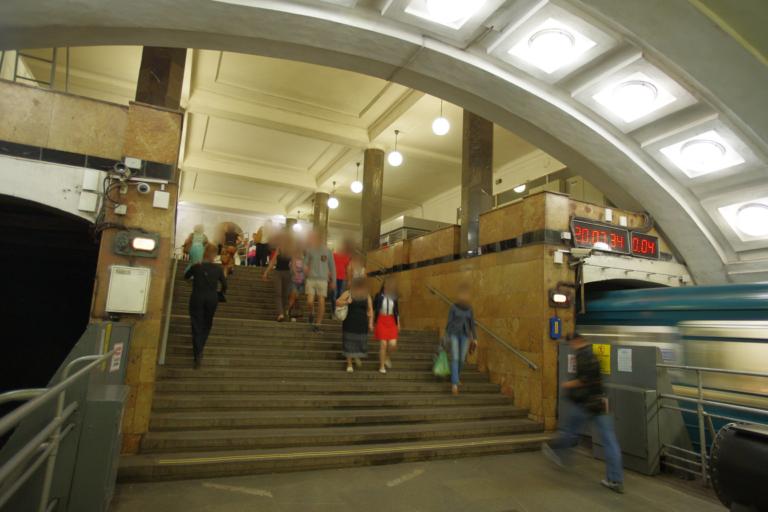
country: RU
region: Moscow
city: Moscow
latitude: 55.7516
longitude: 37.6103
